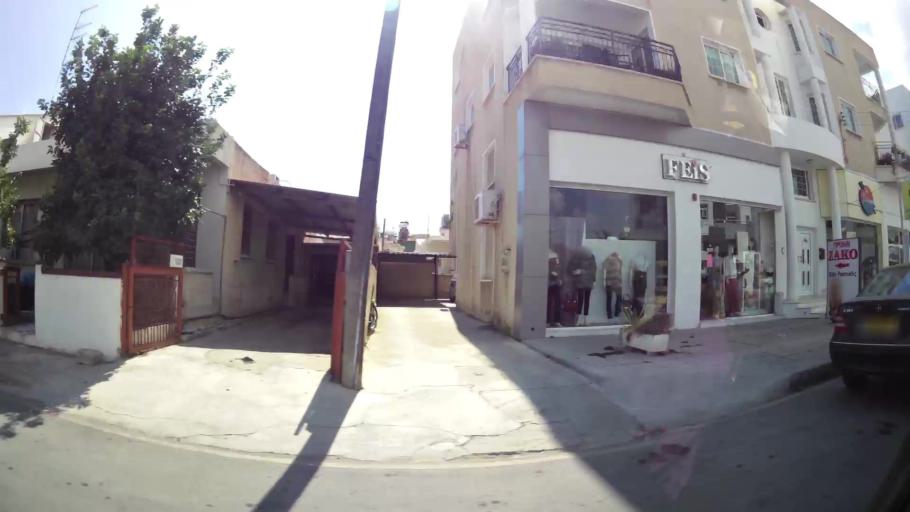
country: CY
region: Larnaka
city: Larnaca
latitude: 34.9109
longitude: 33.6220
